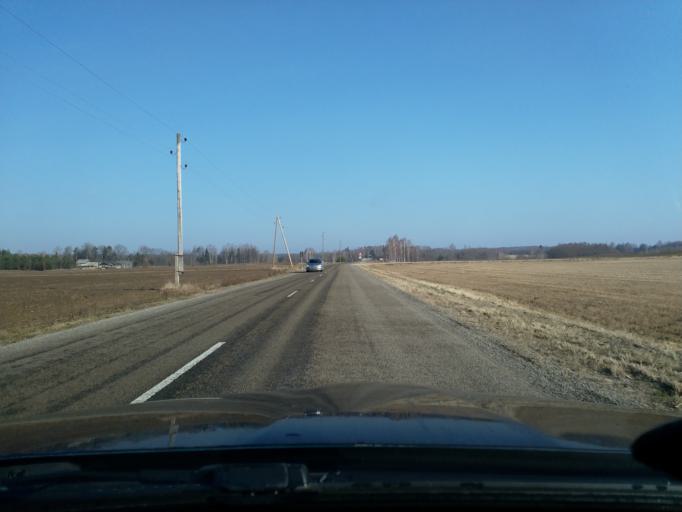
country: LV
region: Kuldigas Rajons
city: Kuldiga
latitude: 56.8758
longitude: 21.9379
